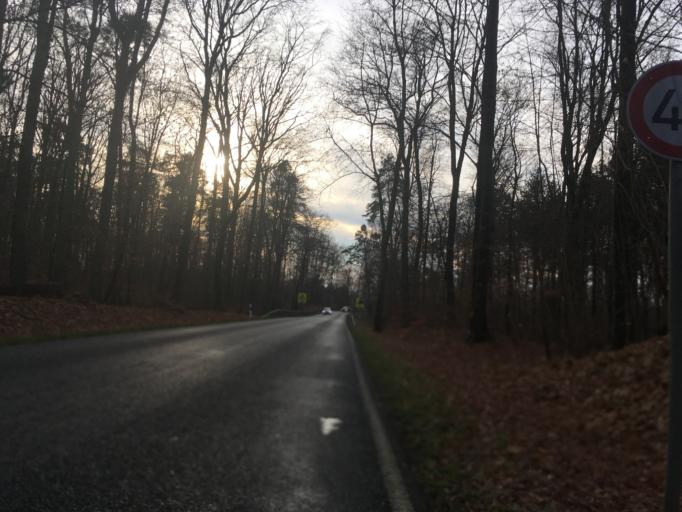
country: DE
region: Brandenburg
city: Eberswalde
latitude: 52.8546
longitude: 13.8576
